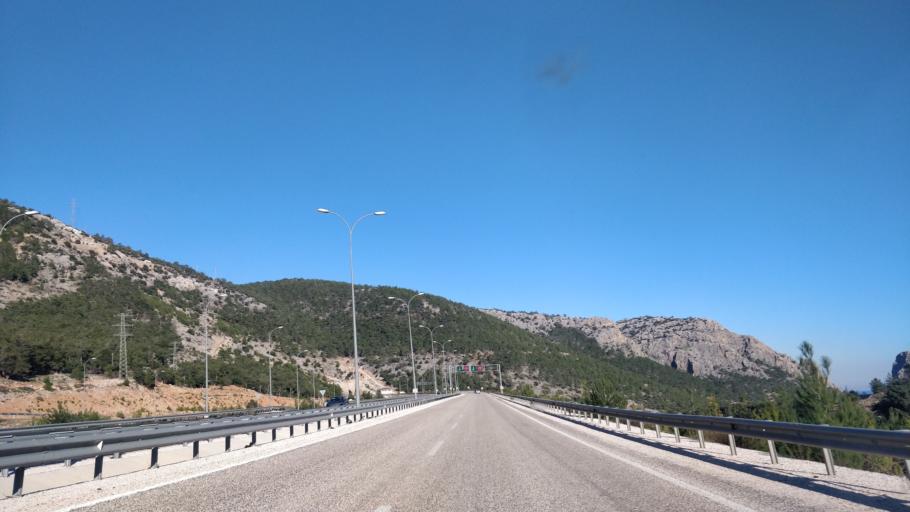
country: TR
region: Mersin
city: Akdere
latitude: 36.2551
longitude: 33.7852
